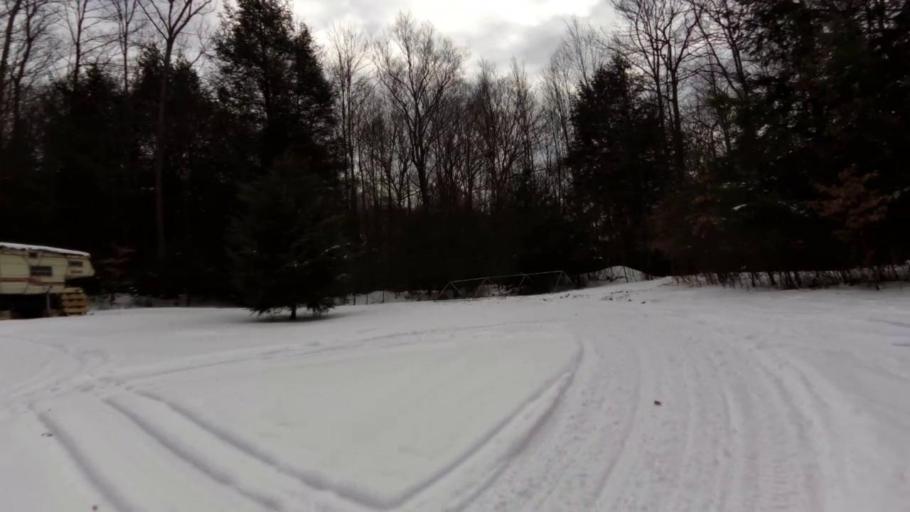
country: US
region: Pennsylvania
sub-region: McKean County
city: Foster Brook
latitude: 42.0093
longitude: -78.5979
